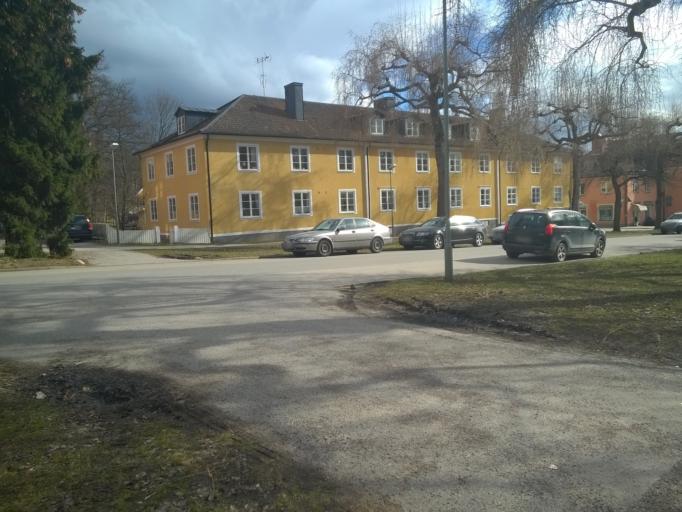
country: SE
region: Stockholm
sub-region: Stockholms Kommun
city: Bromma
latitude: 59.3245
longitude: 17.9569
